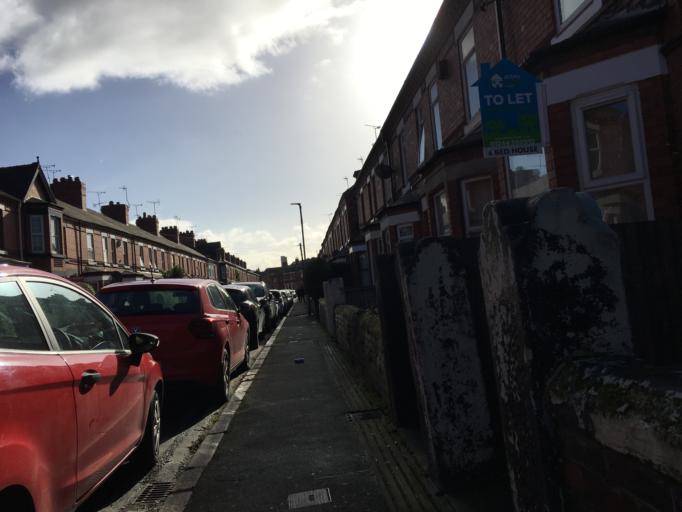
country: GB
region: England
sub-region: Cheshire West and Chester
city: Hoole
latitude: 53.2005
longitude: -2.8828
